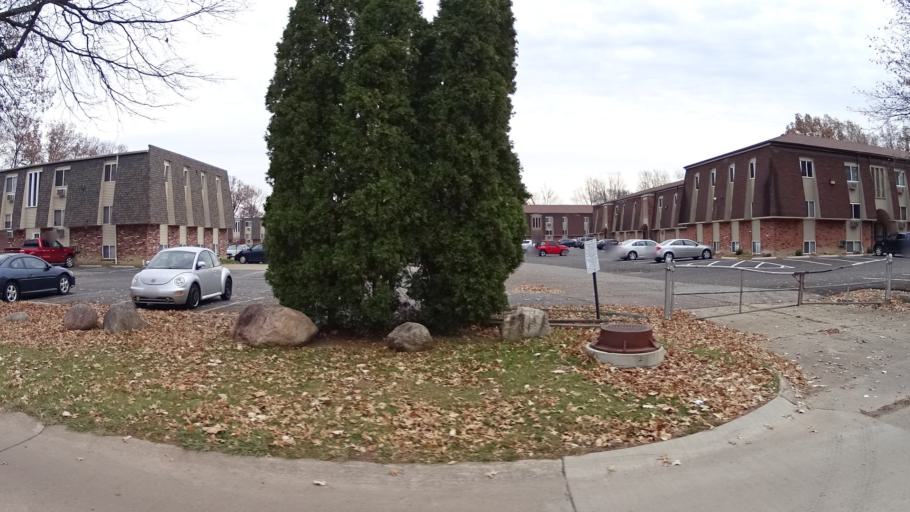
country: US
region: Ohio
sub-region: Lorain County
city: North Ridgeville
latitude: 41.4018
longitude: -82.0090
